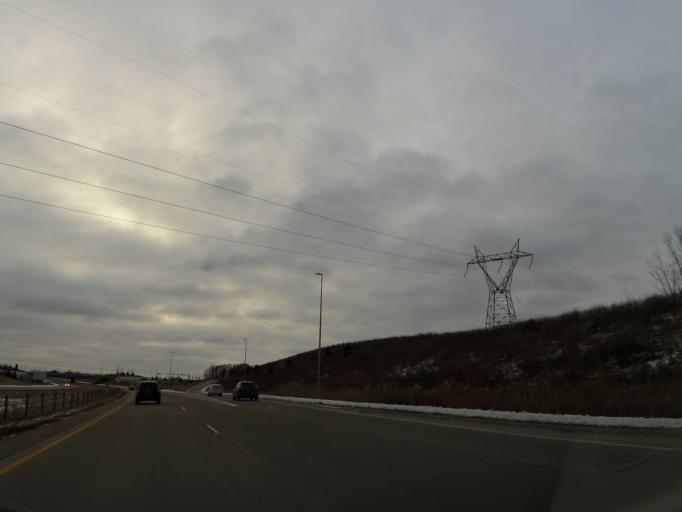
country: US
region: Minnesota
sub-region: Carver County
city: Chaska
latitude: 44.8096
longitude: -93.6219
